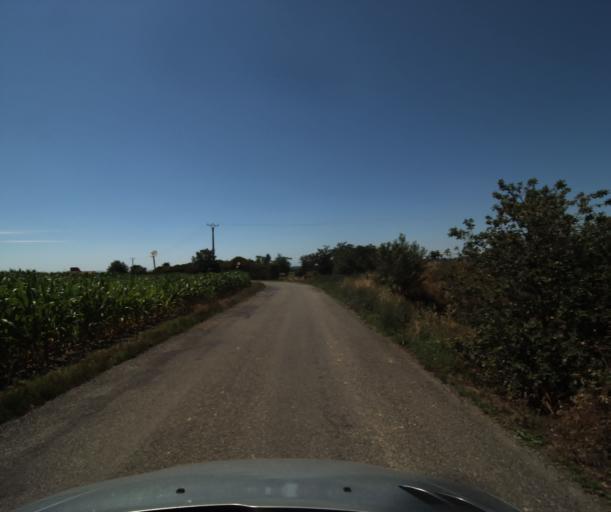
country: FR
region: Midi-Pyrenees
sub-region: Departement de la Haute-Garonne
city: Roquettes
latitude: 43.4899
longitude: 1.3682
